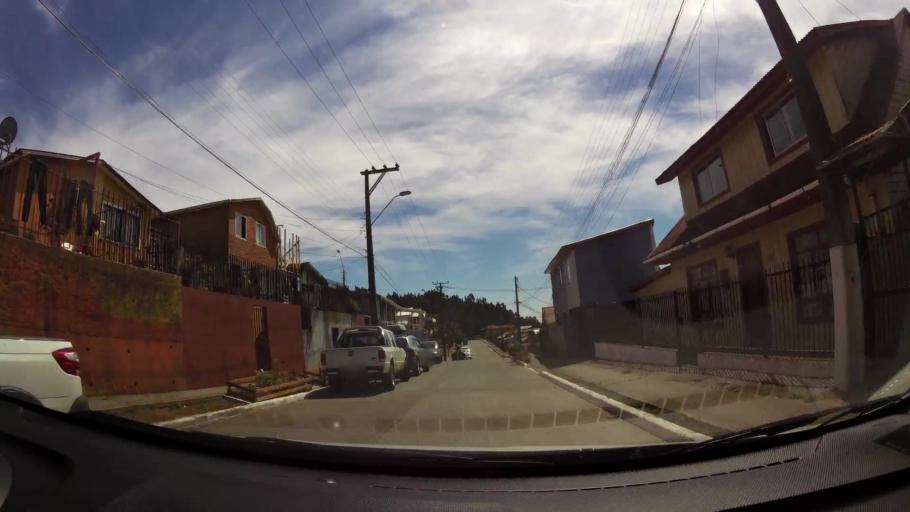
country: CL
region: Biobio
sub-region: Provincia de Concepcion
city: Talcahuano
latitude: -36.7094
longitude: -73.1193
